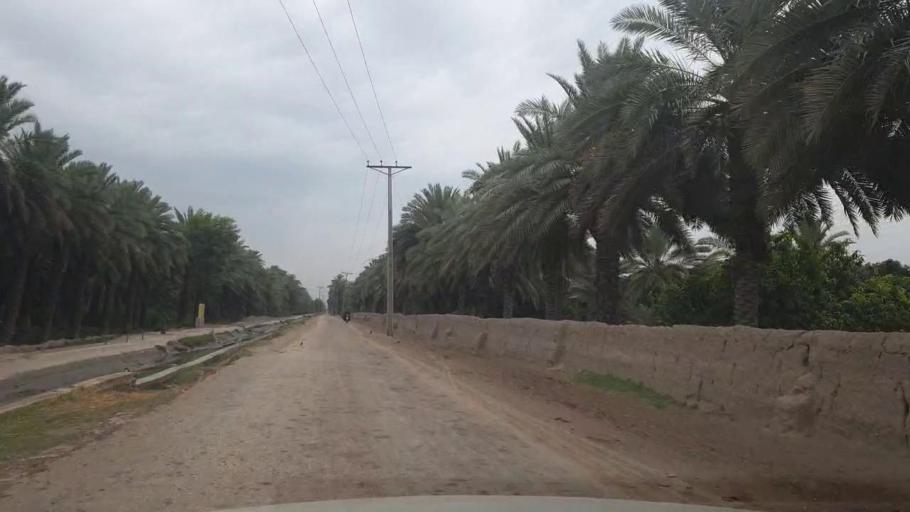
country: PK
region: Sindh
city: Sukkur
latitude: 27.6220
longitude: 68.8195
